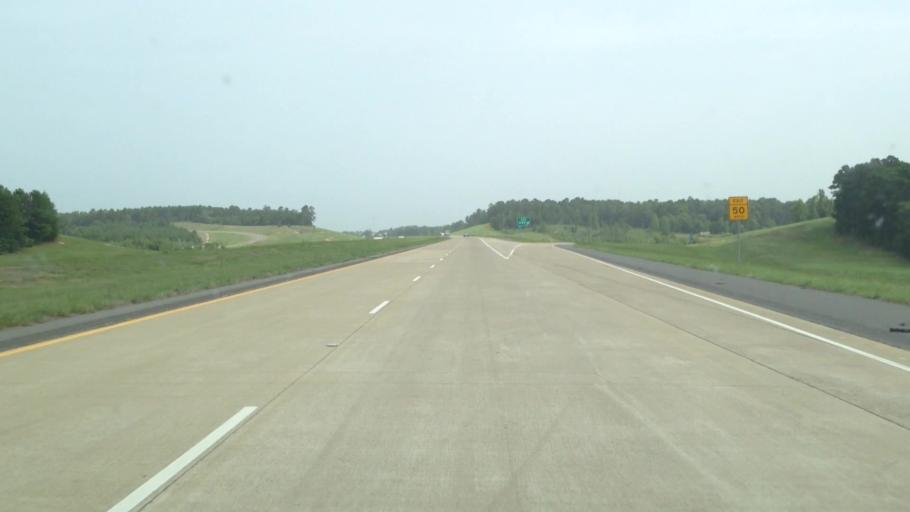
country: US
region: Louisiana
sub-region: Caddo Parish
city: Vivian
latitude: 32.9380
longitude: -93.8969
